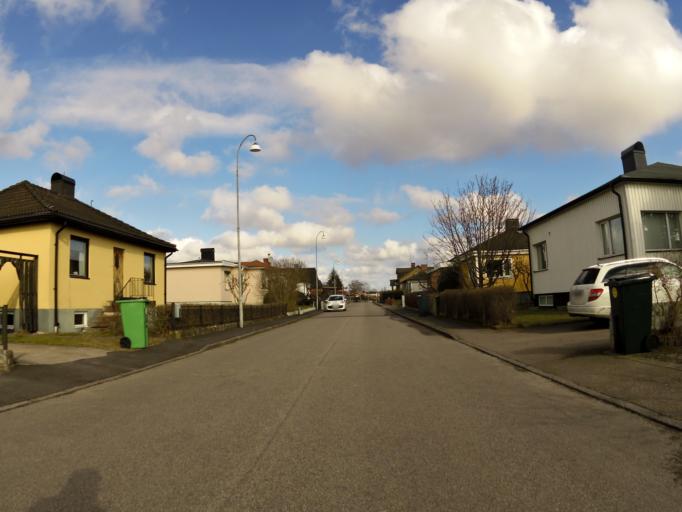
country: SE
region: Halland
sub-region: Halmstads Kommun
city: Halmstad
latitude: 56.6803
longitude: 12.8748
